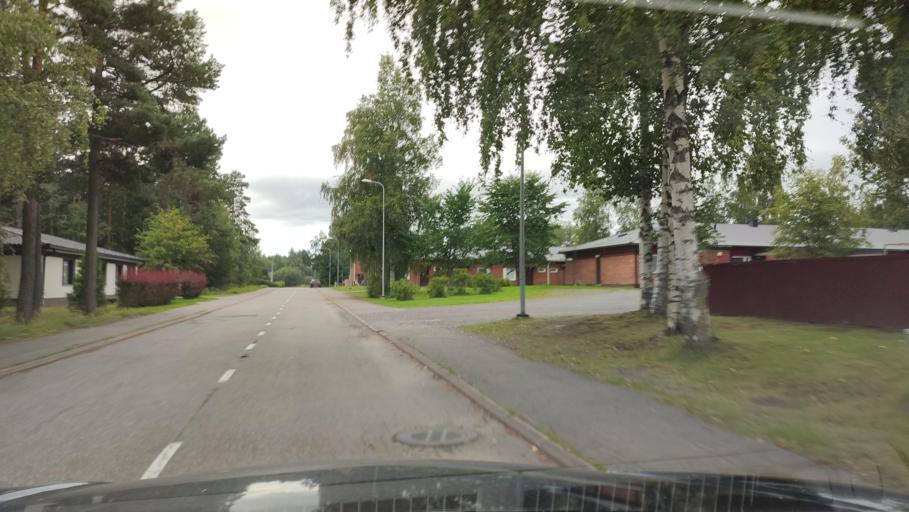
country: FI
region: Ostrobothnia
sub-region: Sydosterbotten
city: Kristinestad
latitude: 62.2669
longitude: 21.3622
